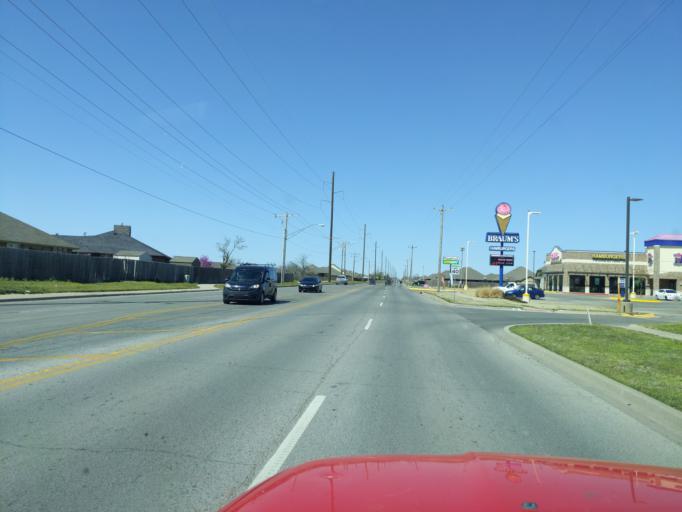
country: US
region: Oklahoma
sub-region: Cleveland County
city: Moore
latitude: 35.3203
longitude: -97.5120
